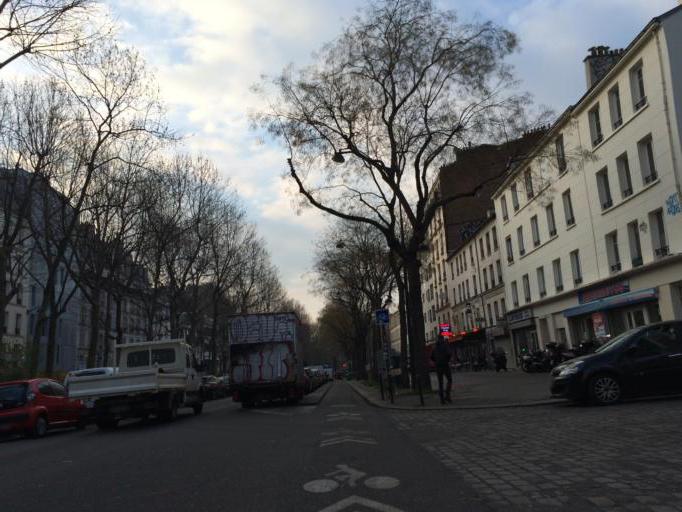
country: FR
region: Ile-de-France
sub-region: Paris
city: Paris
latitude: 48.8763
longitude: 2.3723
